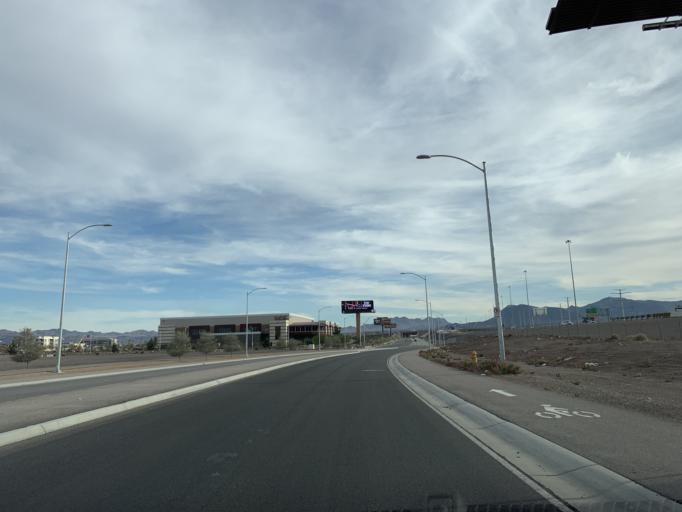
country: US
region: Nevada
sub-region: Clark County
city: Whitney
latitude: 36.0784
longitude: -115.0404
